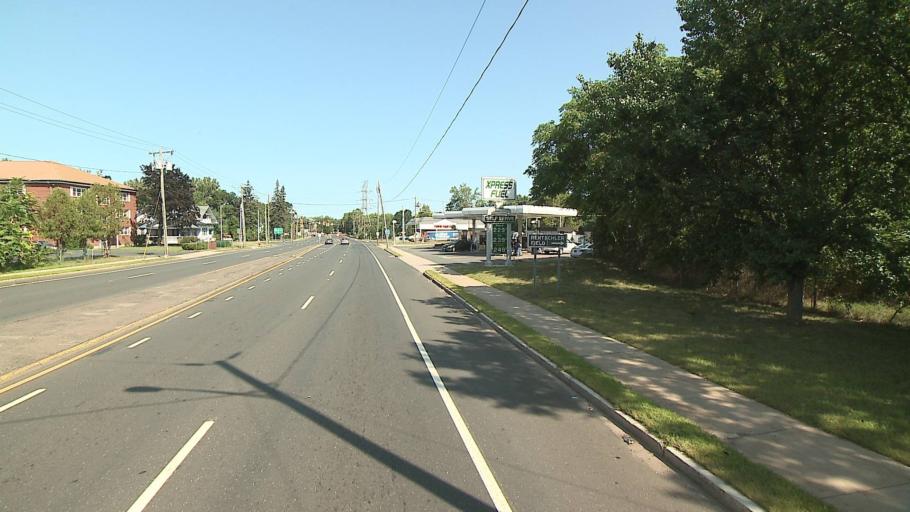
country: US
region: Connecticut
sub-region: Hartford County
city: East Hartford
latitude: 41.7593
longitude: -72.6440
